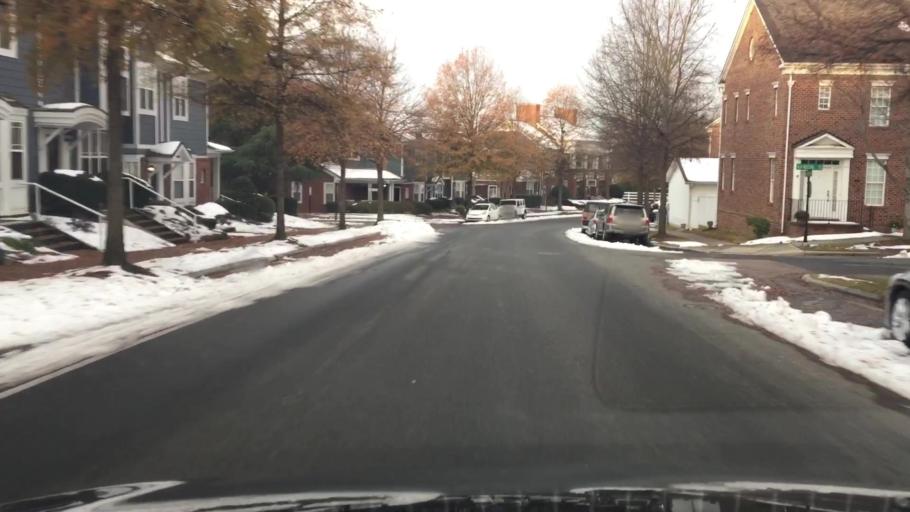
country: US
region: North Carolina
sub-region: Mecklenburg County
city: Cornelius
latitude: 35.4988
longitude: -80.8616
